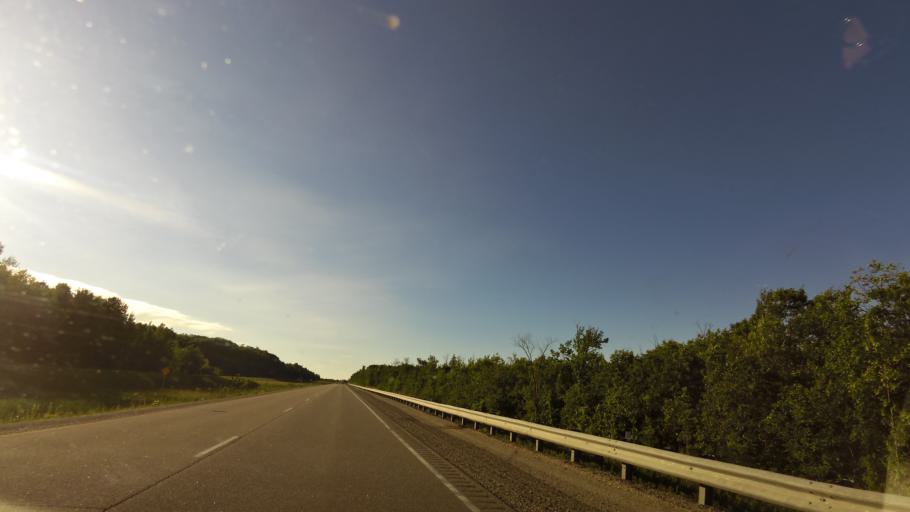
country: CA
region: Ontario
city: Midland
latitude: 44.7215
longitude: -79.6731
